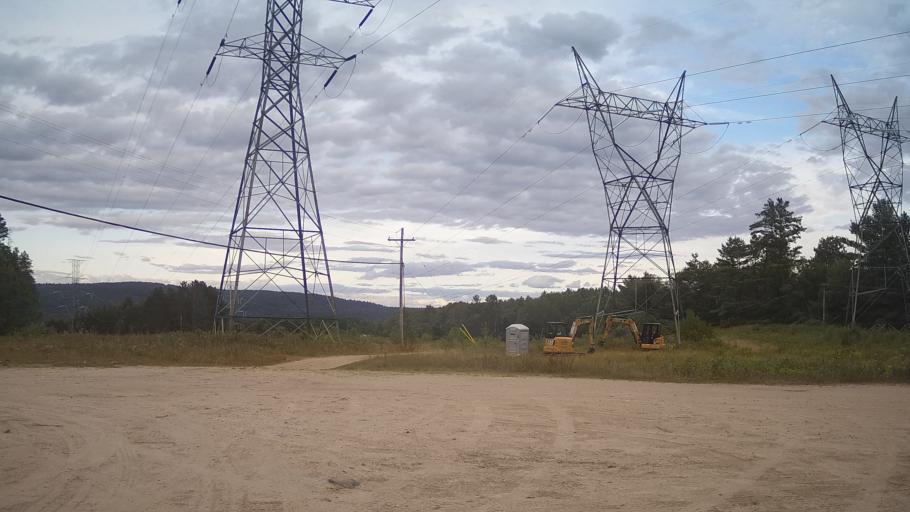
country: CA
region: Ontario
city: Deep River
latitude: 46.1714
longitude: -77.6967
